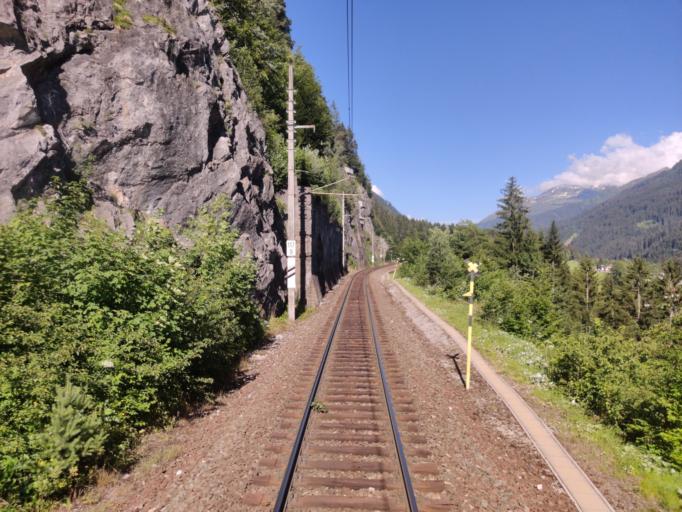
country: AT
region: Vorarlberg
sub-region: Politischer Bezirk Bludenz
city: Dalaas
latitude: 47.1327
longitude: 10.0317
